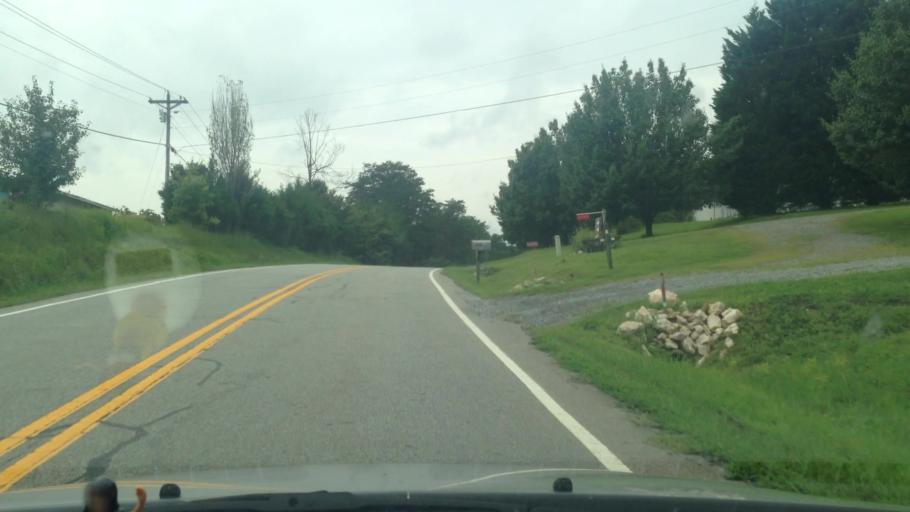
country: US
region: North Carolina
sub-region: Stokes County
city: Danbury
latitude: 36.4074
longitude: -80.1187
